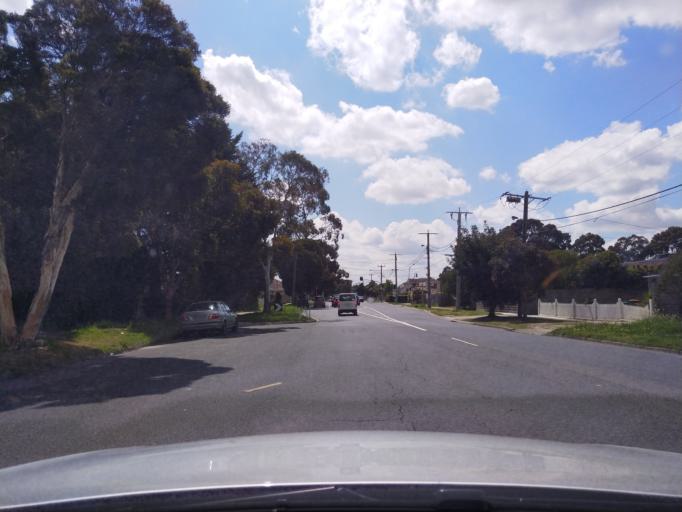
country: AU
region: Victoria
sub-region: Banyule
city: Heidelberg Heights
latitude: -37.7433
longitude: 145.0476
